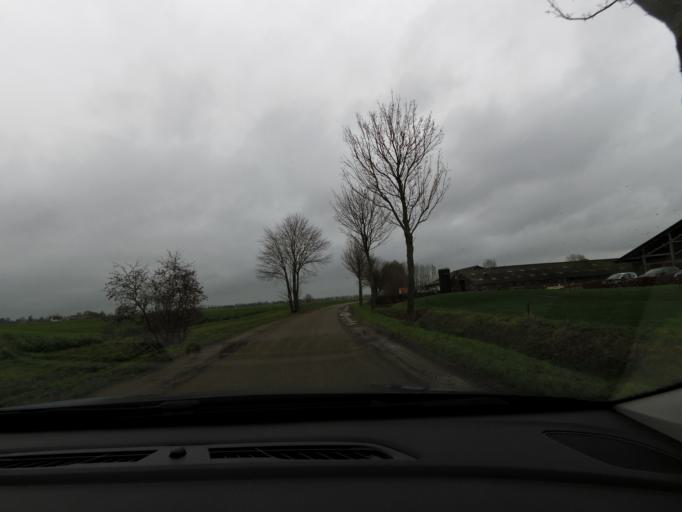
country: NL
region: North Brabant
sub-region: Gemeente Waalwijk
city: Waalwijk
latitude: 51.7494
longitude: 5.0450
